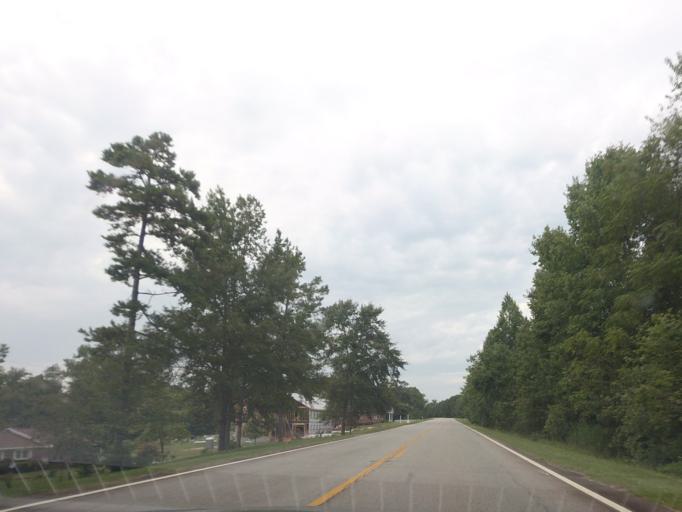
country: US
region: Georgia
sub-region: Twiggs County
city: Jeffersonville
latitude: 32.7305
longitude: -83.4187
